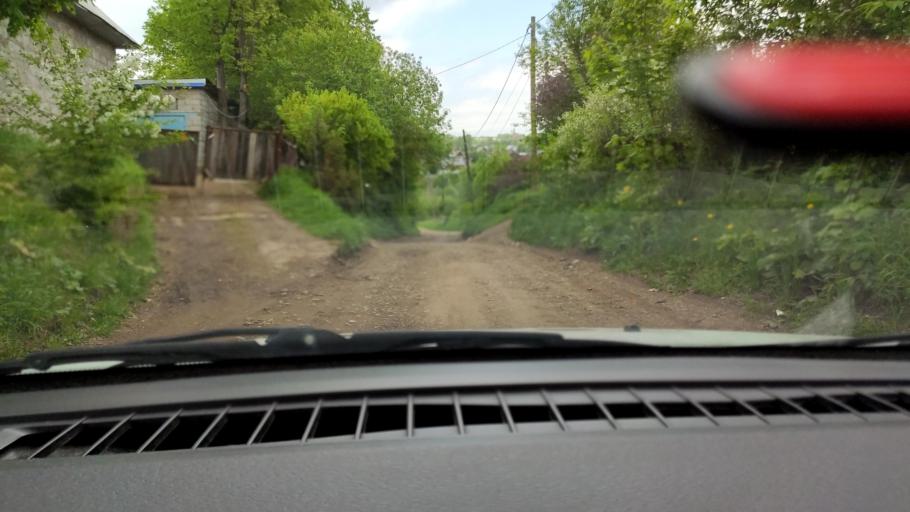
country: RU
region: Perm
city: Bershet'
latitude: 57.7269
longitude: 56.3840
